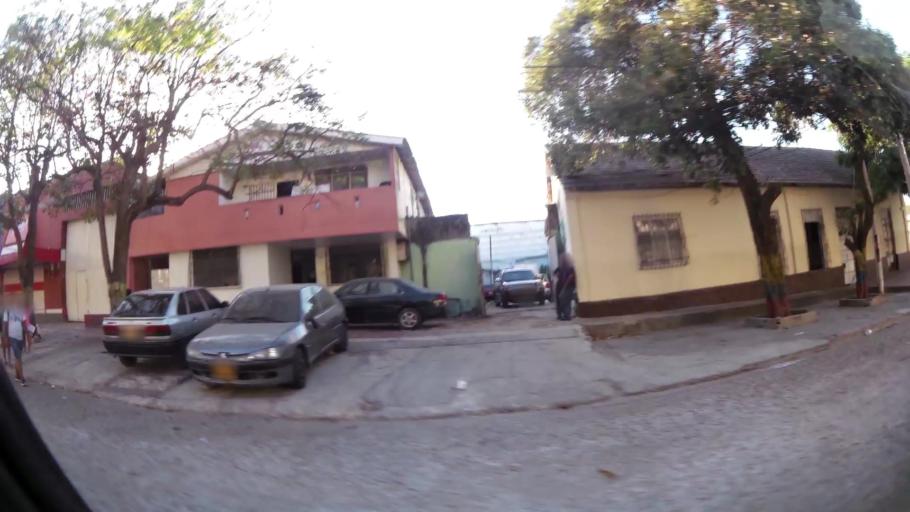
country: CO
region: Atlantico
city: Barranquilla
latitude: 10.9830
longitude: -74.7908
